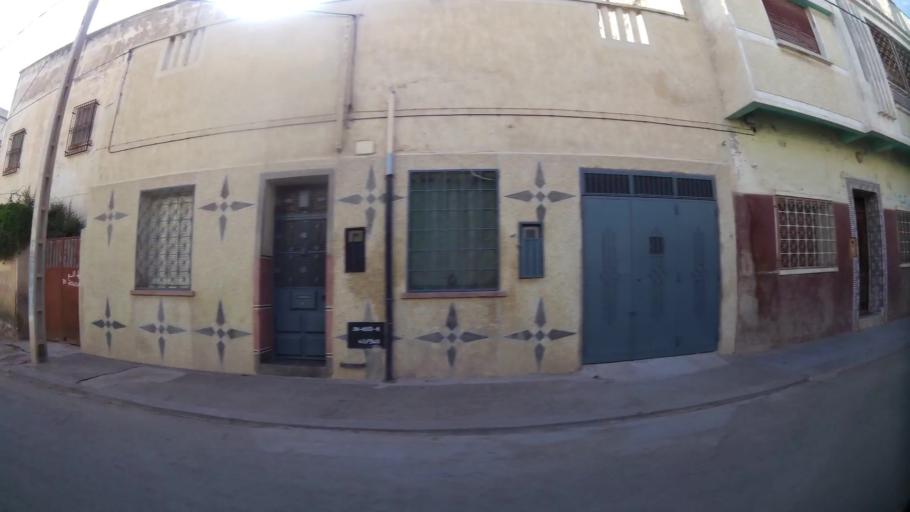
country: MA
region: Oriental
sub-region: Oujda-Angad
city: Oujda
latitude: 34.6714
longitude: -1.9237
